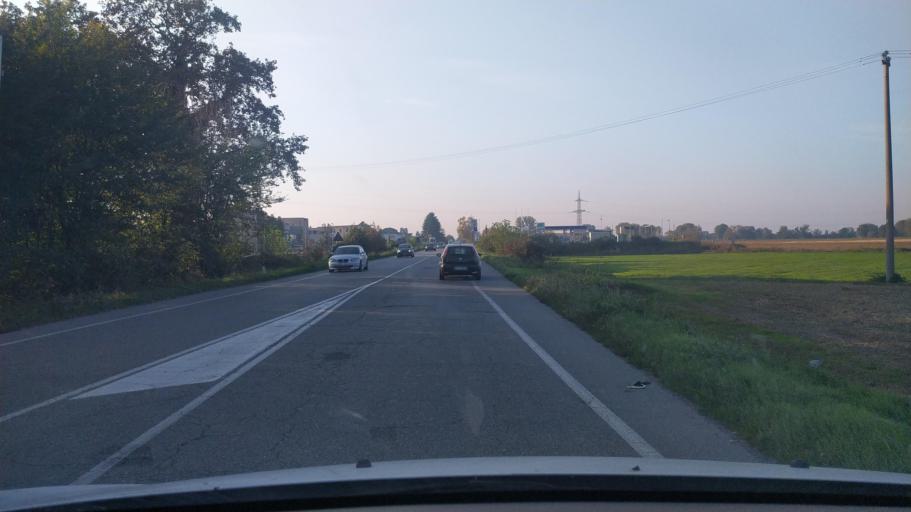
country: IT
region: Lombardy
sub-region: Provincia di Lodi
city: Zelo Buon Persico
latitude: 45.4079
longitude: 9.4449
